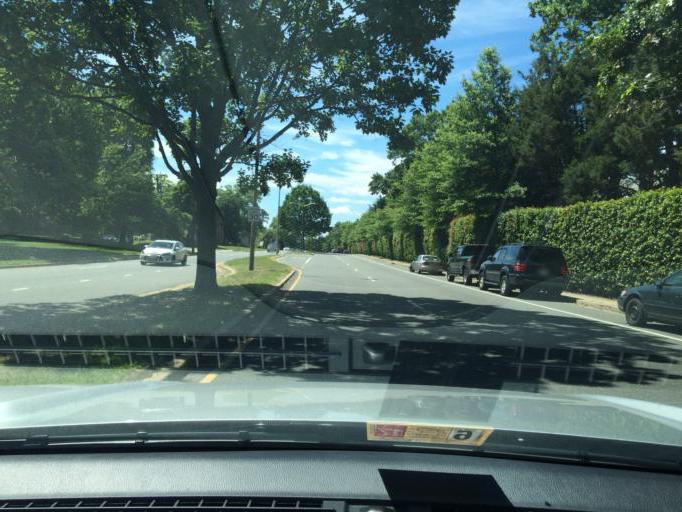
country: US
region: Virginia
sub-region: Fairfax County
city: Huntington
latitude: 38.8347
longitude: -77.0854
